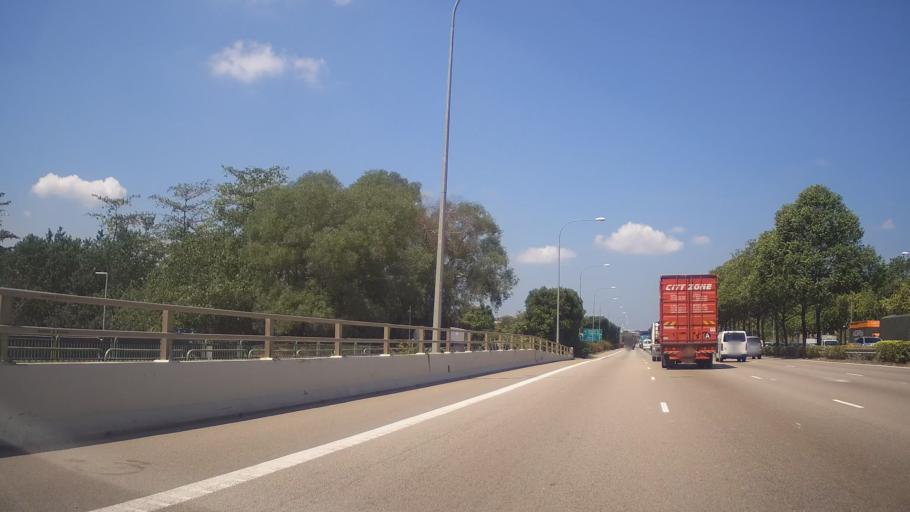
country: SG
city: Singapore
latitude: 1.3266
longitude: 103.7334
